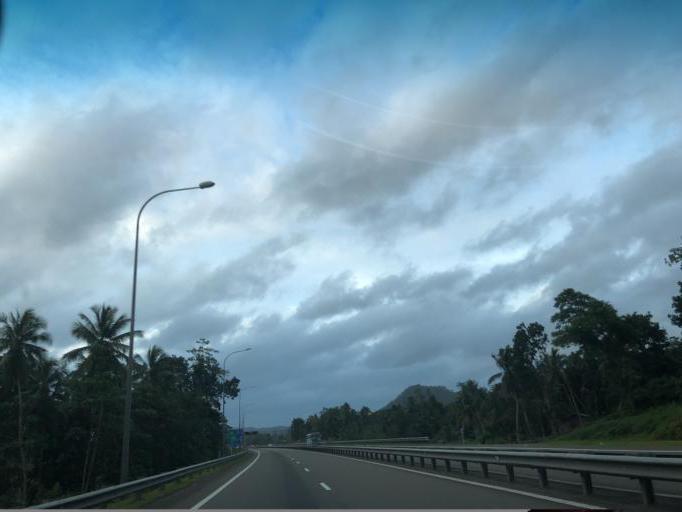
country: LK
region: Western
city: Horawala Junction
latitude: 6.4441
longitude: 80.0925
